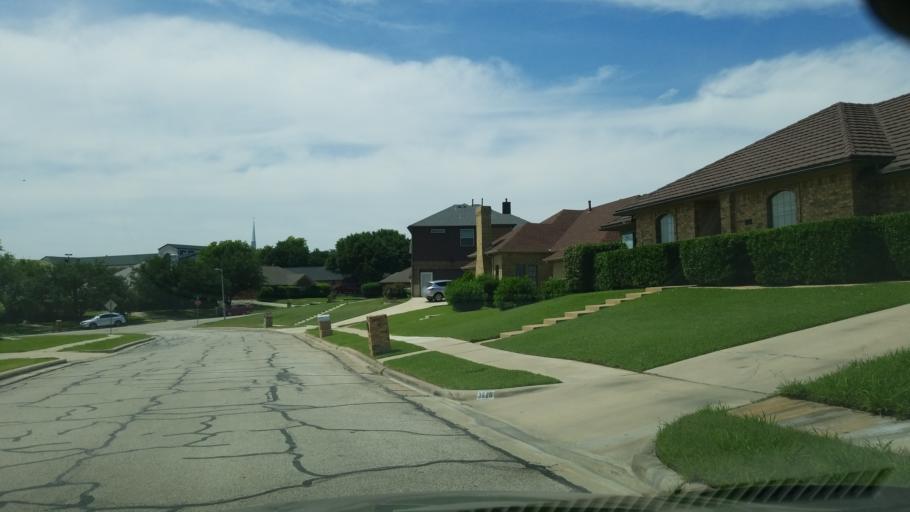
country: US
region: Texas
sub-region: Dallas County
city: Irving
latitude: 32.8757
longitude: -96.9973
